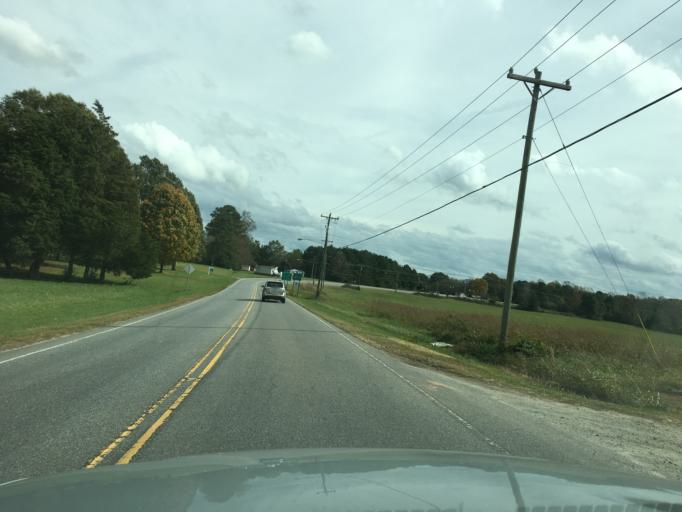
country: US
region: North Carolina
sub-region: Catawba County
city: Newton
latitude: 35.6595
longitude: -81.2701
